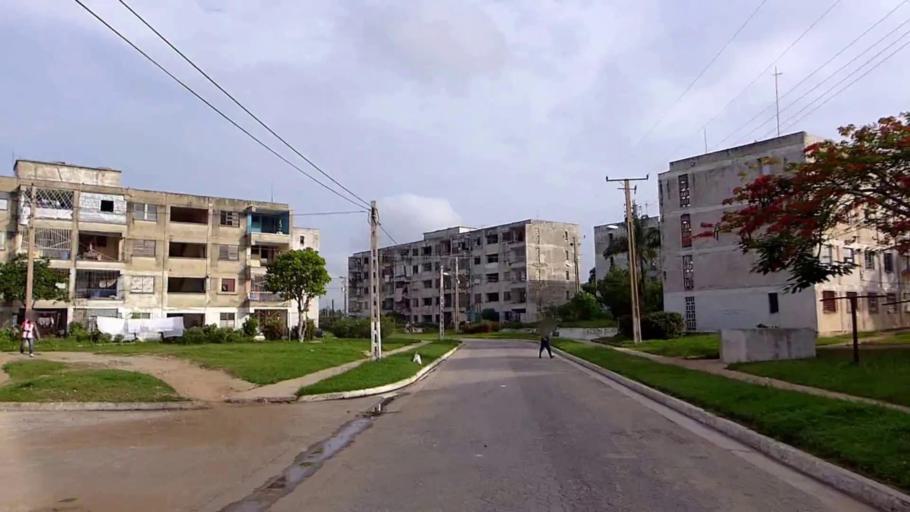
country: CU
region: Camaguey
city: Camaguey
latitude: 21.3843
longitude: -77.9378
